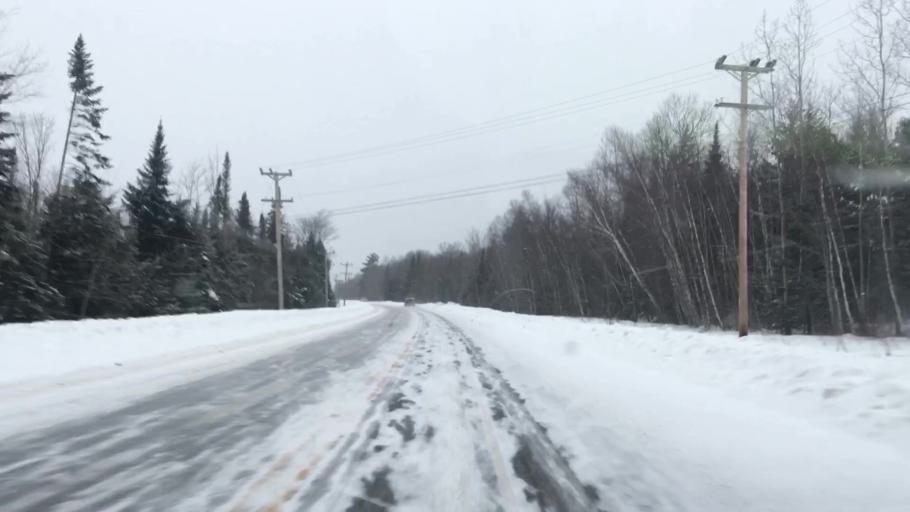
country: US
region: Maine
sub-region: Penobscot County
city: Medway
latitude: 45.5840
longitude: -68.4275
